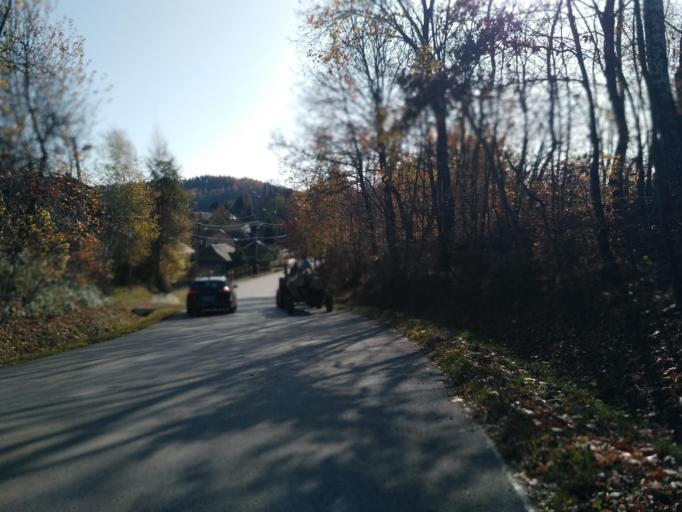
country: PL
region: Subcarpathian Voivodeship
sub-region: Powiat brzozowski
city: Nozdrzec
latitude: 49.8158
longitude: 22.1666
